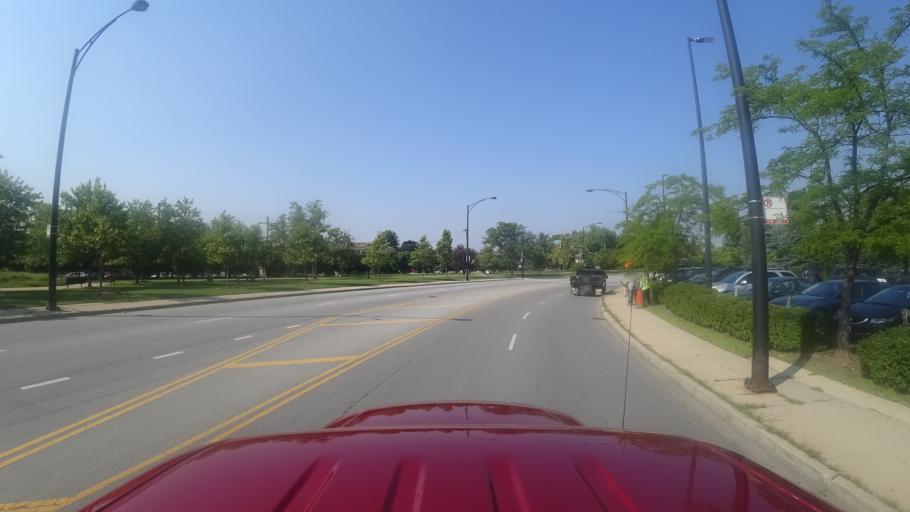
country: US
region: Illinois
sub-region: Cook County
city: Hometown
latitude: 41.7846
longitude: -87.7393
